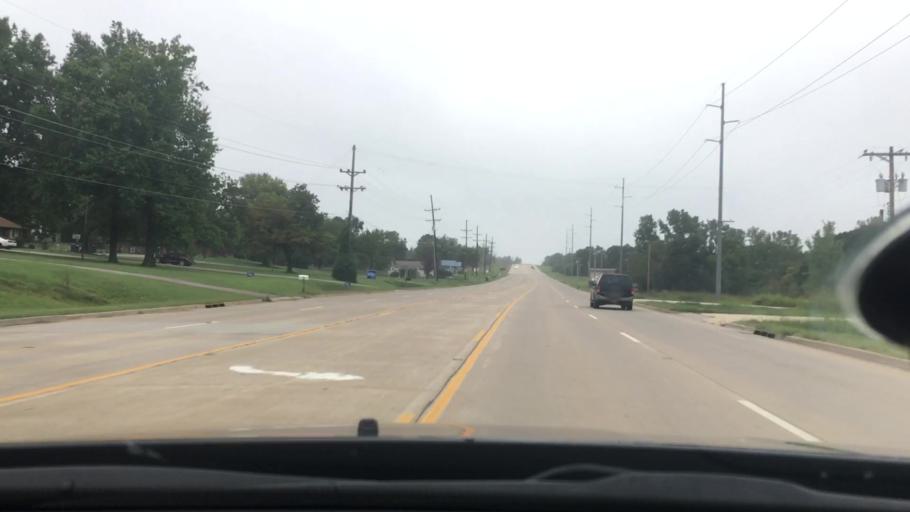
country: US
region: Oklahoma
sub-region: Seminole County
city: Seminole
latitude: 35.2564
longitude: -96.6711
